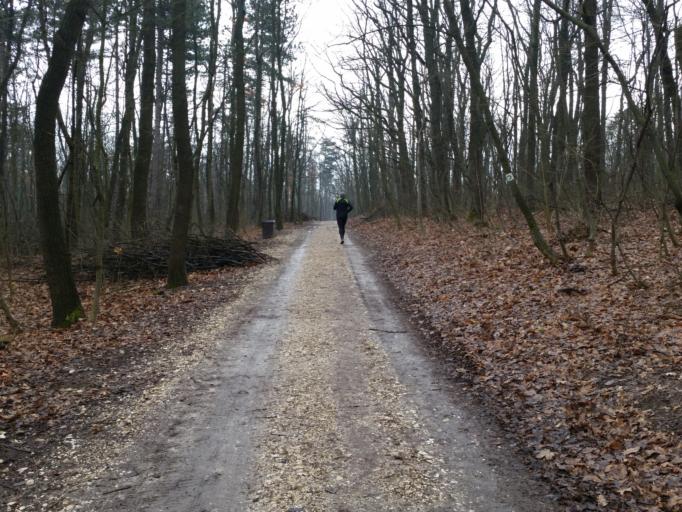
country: HU
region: Budapest
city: Budapest II. keruelet
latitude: 47.5433
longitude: 18.9926
